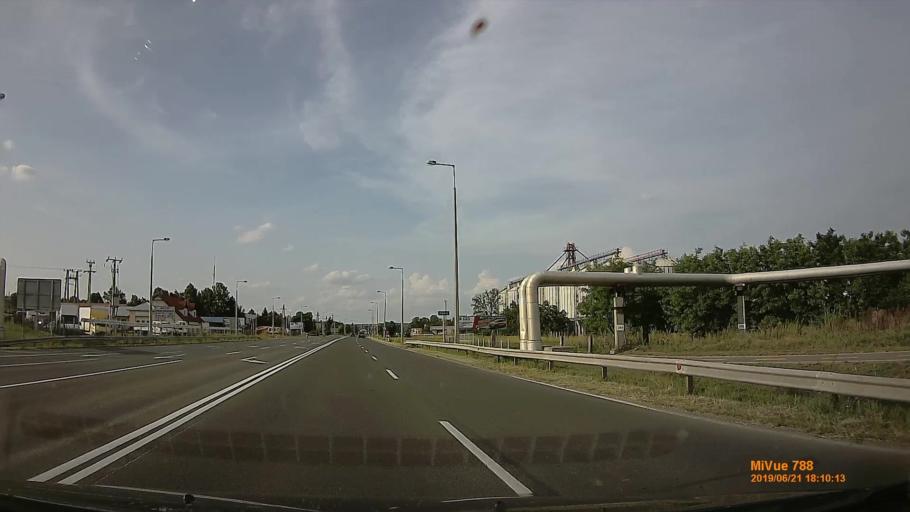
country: HU
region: Tolna
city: Paks
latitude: 46.6020
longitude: 18.8469
